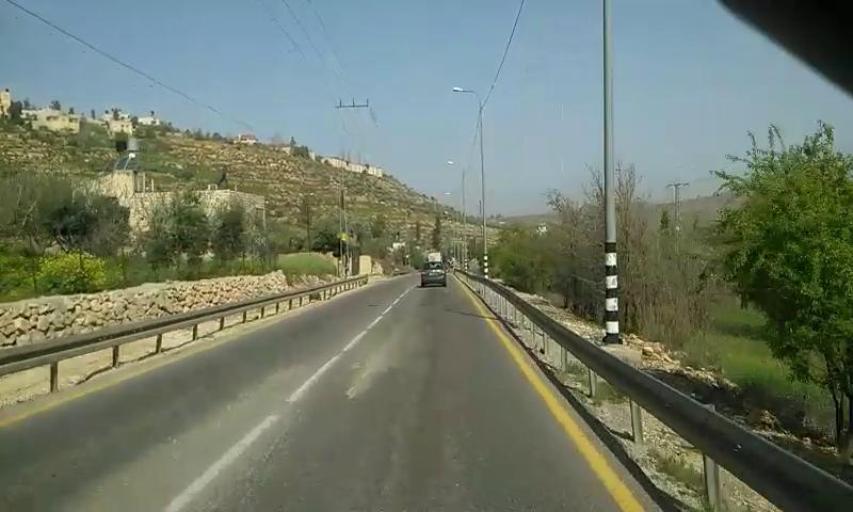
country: PS
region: West Bank
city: Sinjil
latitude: 32.0329
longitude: 35.2712
